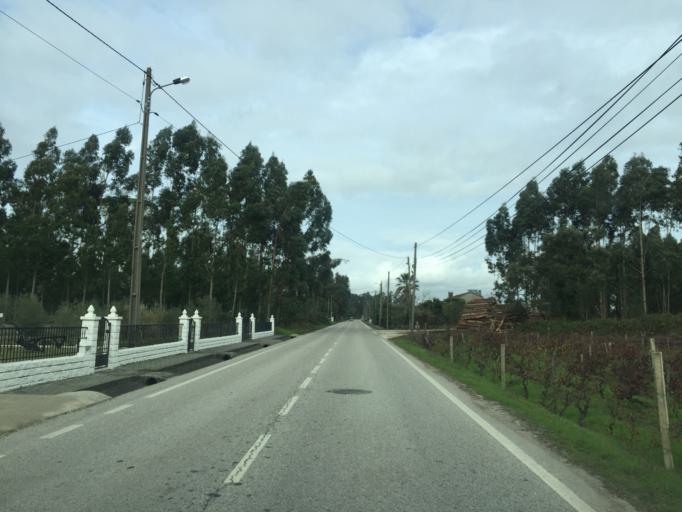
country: PT
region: Coimbra
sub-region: Figueira da Foz
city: Lavos
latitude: 40.0408
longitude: -8.8190
